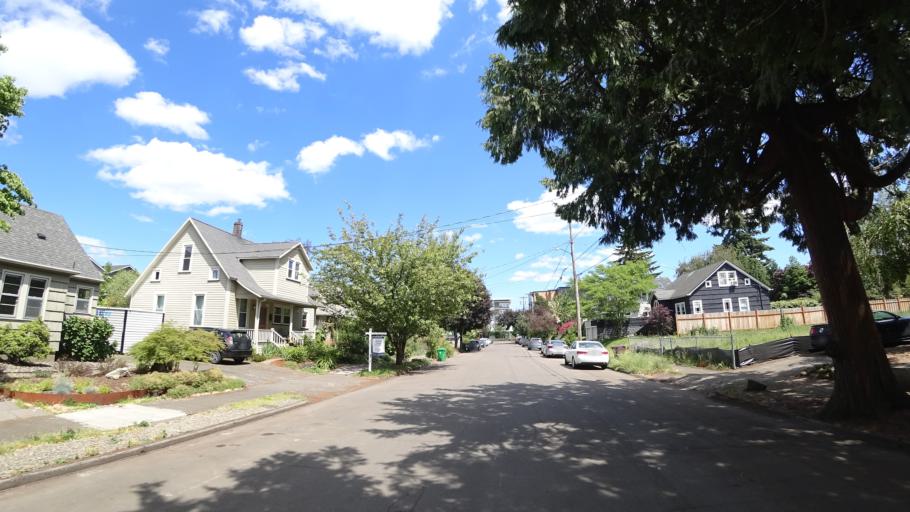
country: US
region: Oregon
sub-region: Multnomah County
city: Portland
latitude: 45.5606
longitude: -122.6841
